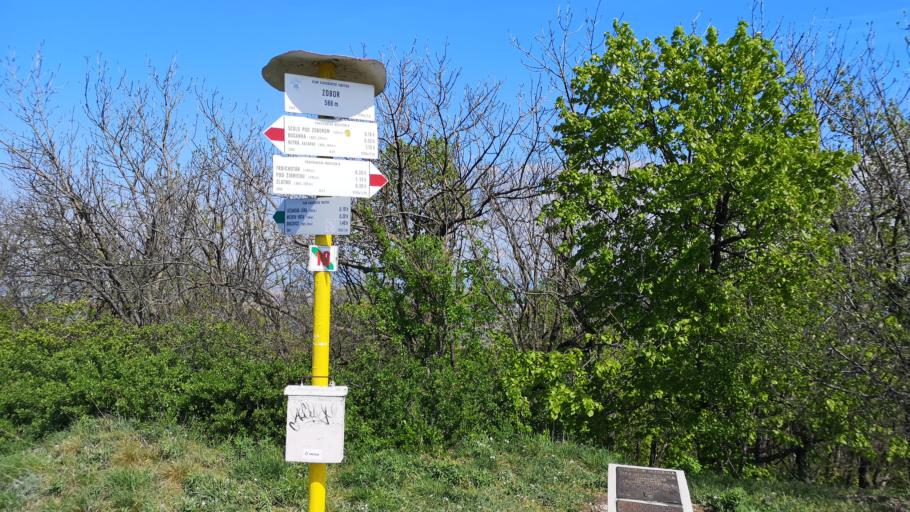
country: SK
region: Nitriansky
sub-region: Okres Nitra
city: Nitra
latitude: 48.3464
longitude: 18.1089
